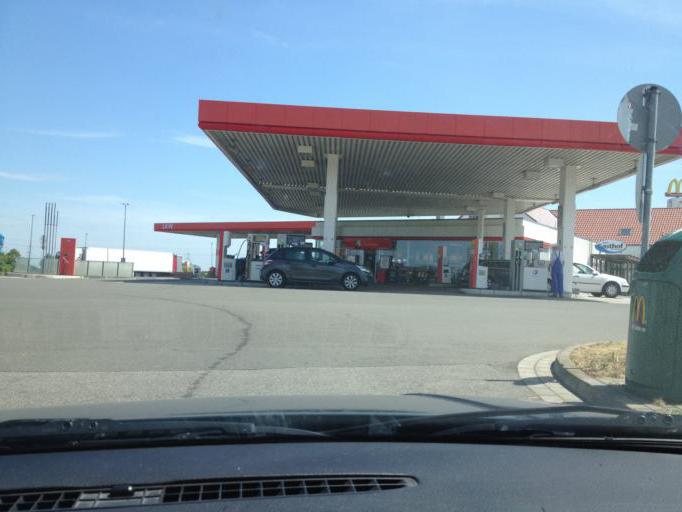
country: DE
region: Rheinland-Pfalz
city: Kirchheim an der Weinstrasse
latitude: 49.5542
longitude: 8.1849
